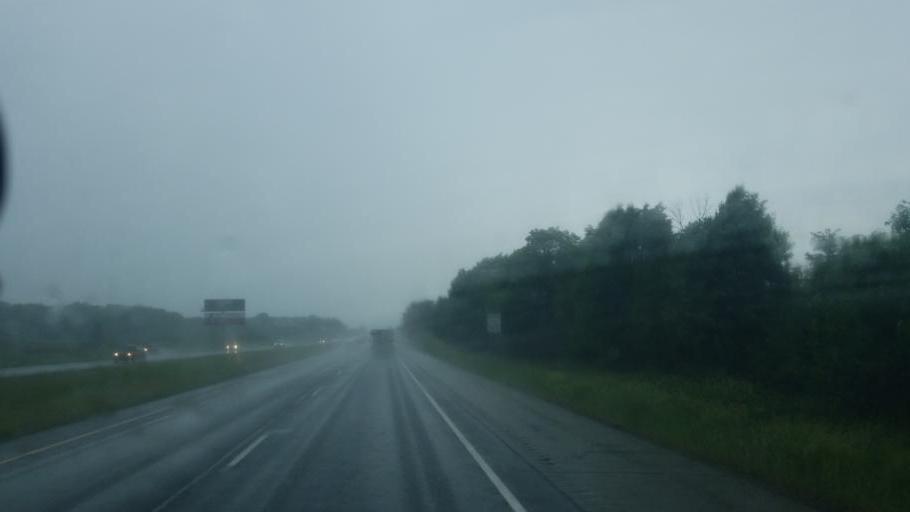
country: US
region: Indiana
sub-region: Whitley County
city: Columbia City
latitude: 41.1369
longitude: -85.4181
